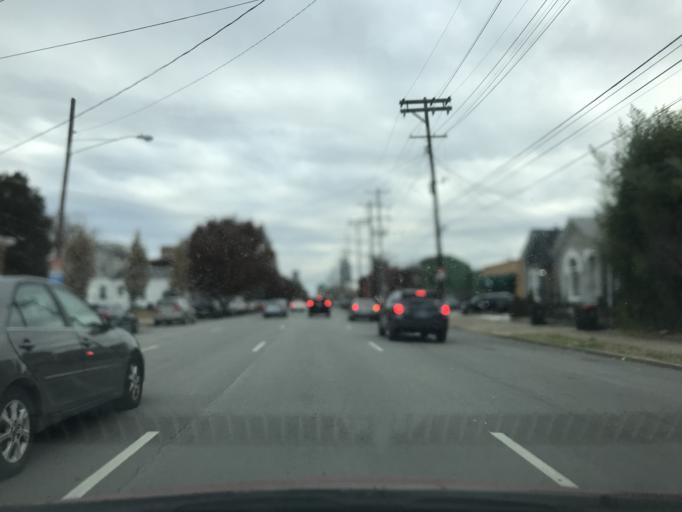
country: US
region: Kentucky
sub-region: Jefferson County
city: Louisville
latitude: 38.2514
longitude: -85.7347
